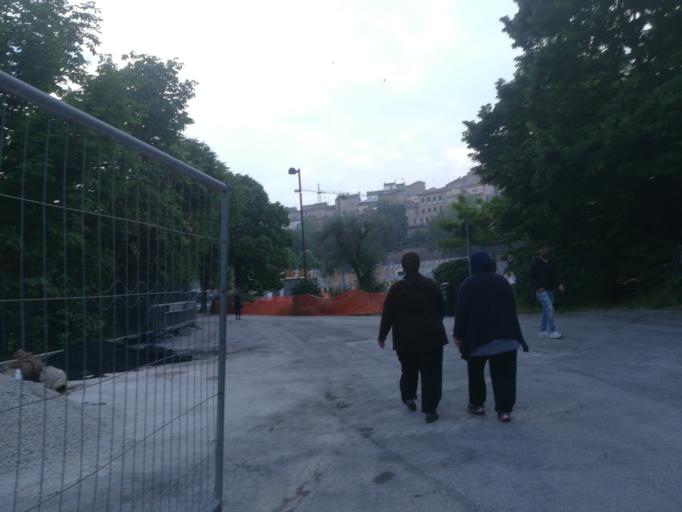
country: IT
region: The Marches
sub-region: Provincia di Macerata
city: Macerata
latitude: 43.2990
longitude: 13.4471
